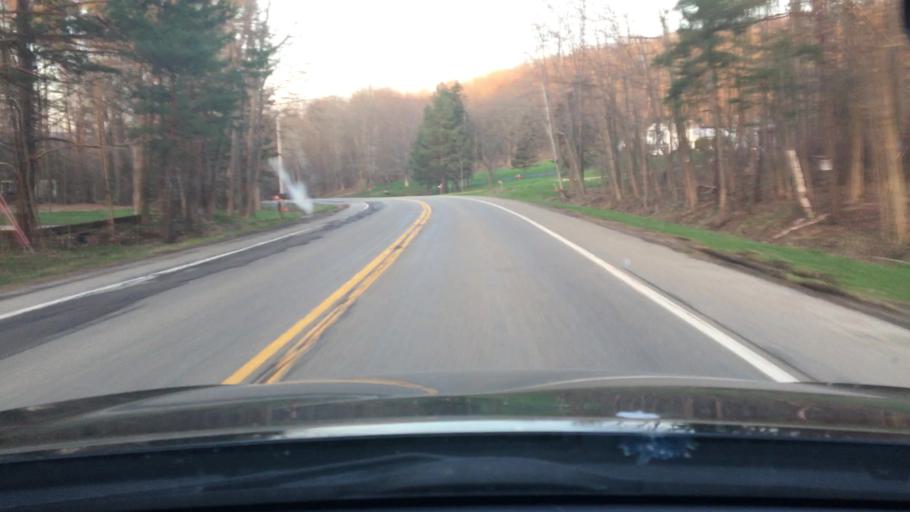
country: US
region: New York
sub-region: Cattaraugus County
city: Randolph
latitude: 42.1749
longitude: -78.9324
